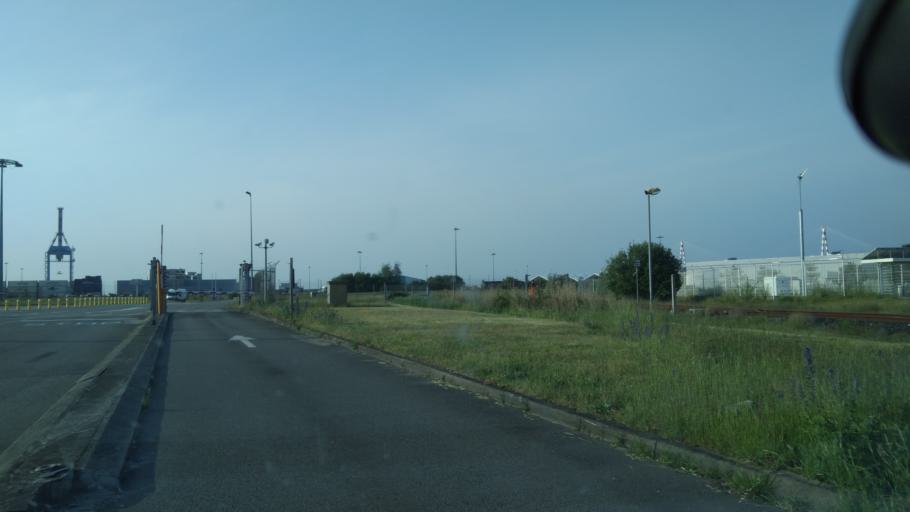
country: FR
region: Pays de la Loire
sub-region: Departement de la Loire-Atlantique
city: Trignac
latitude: 47.3002
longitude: -2.1640
